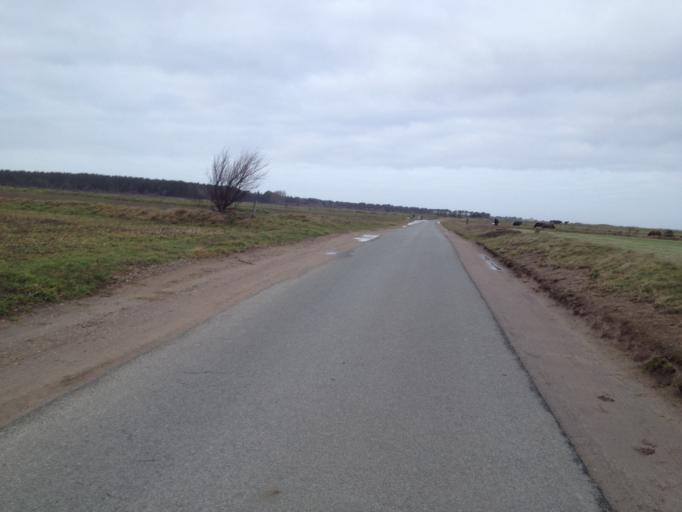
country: DE
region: Schleswig-Holstein
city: Nebel
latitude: 54.6580
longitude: 8.3504
